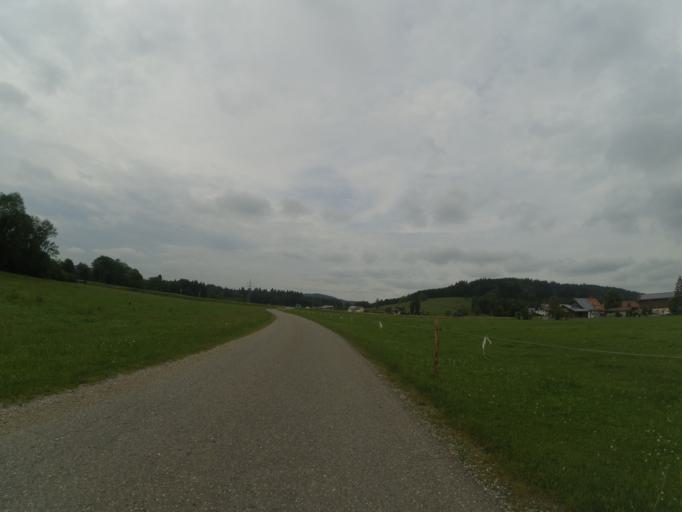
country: DE
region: Baden-Wuerttemberg
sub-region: Tuebingen Region
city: Isny im Allgau
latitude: 47.7151
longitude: 10.0557
